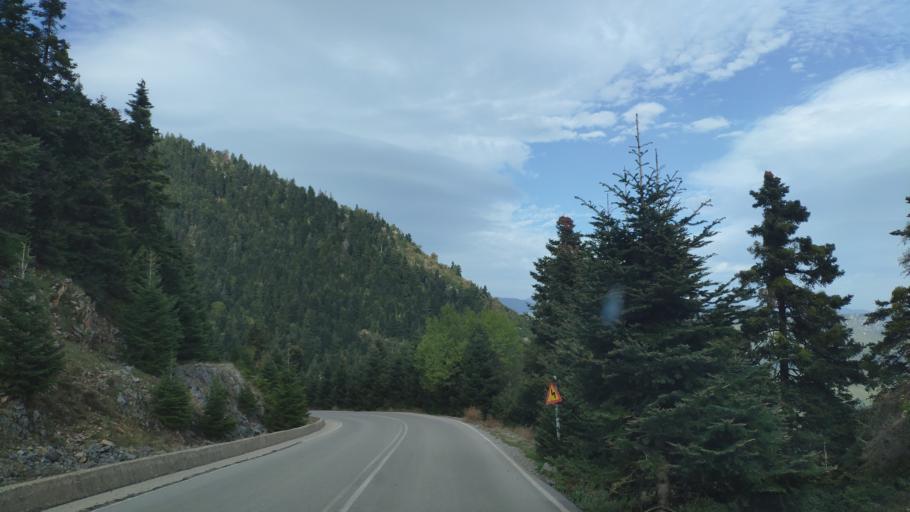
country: GR
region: Central Greece
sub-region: Nomos Fokidos
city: Amfissa
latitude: 38.6625
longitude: 22.3800
